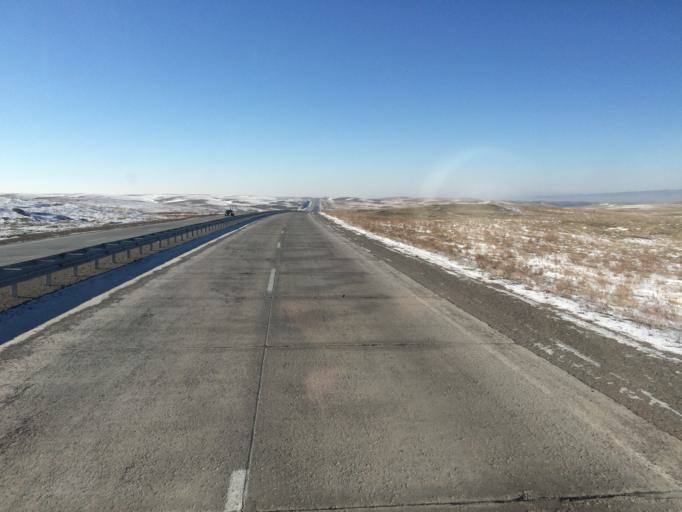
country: KZ
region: Zhambyl
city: Georgiyevka
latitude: 43.3647
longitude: 74.7126
